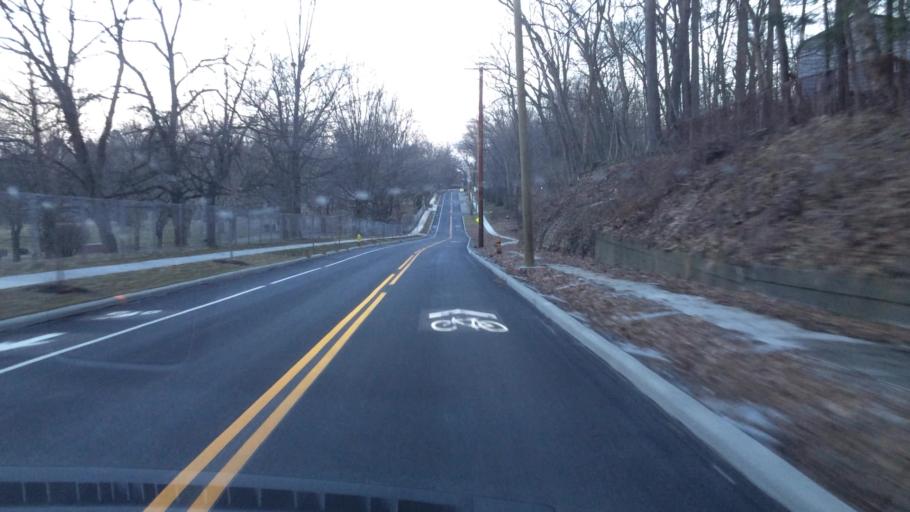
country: US
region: Ohio
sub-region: Summit County
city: Akron
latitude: 41.0994
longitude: -81.5361
